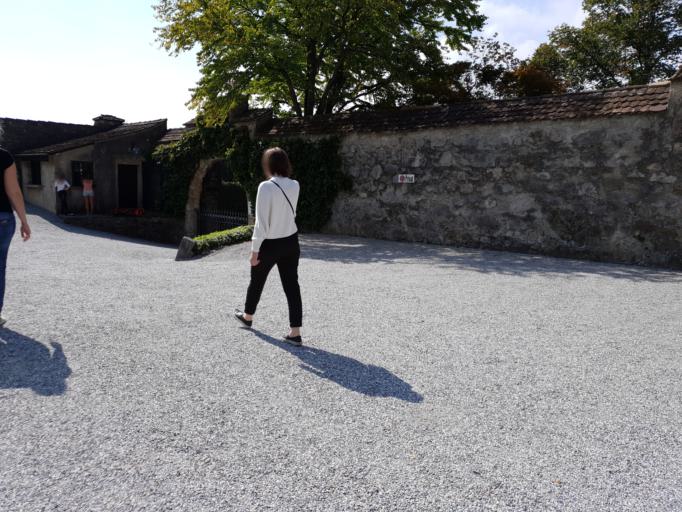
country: LI
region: Vaduz
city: Vaduz
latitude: 47.1392
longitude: 9.5247
